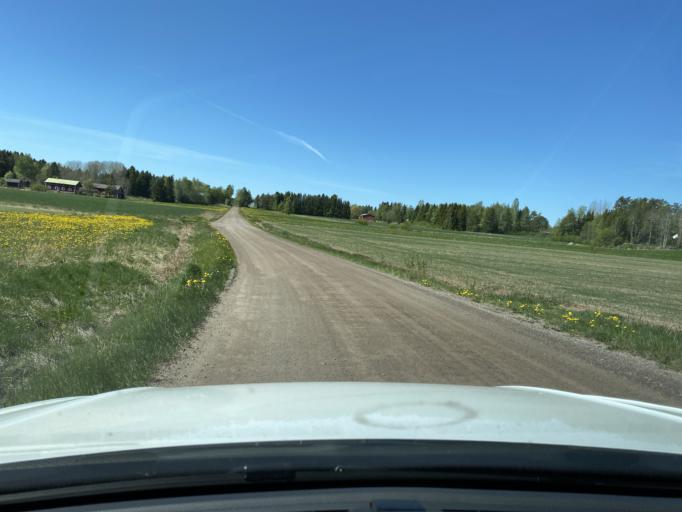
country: FI
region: Satakunta
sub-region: Rauma
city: Lappi
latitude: 61.1380
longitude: 21.9634
